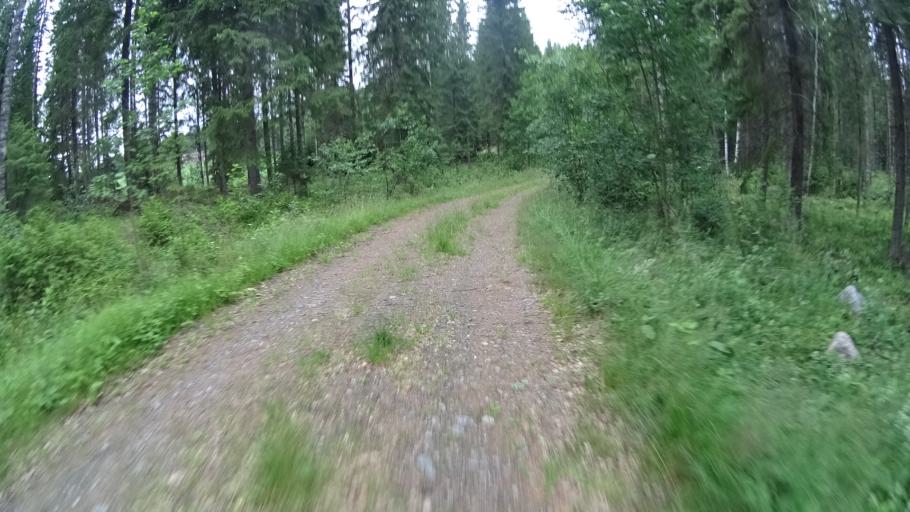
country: FI
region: Uusimaa
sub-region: Helsinki
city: Karkkila
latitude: 60.5678
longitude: 24.3304
